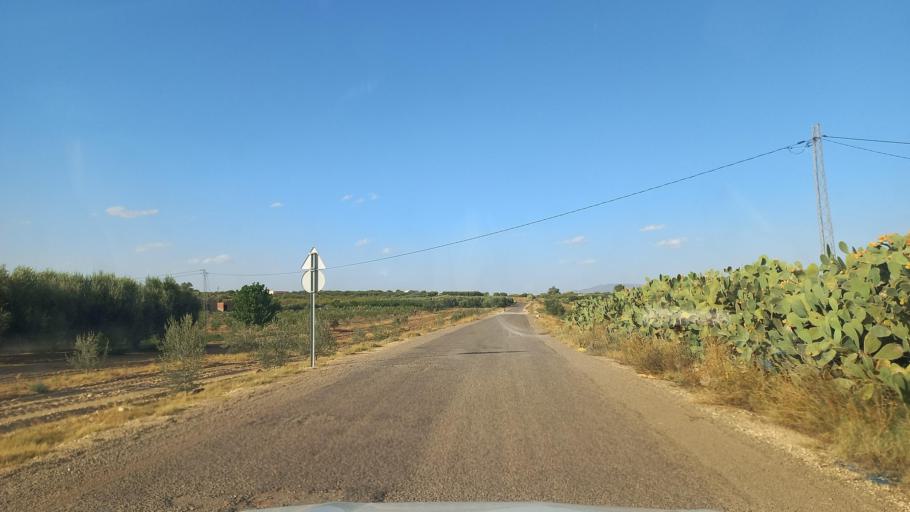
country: TN
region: Al Qasrayn
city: Kasserine
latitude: 35.2668
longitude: 9.0274
